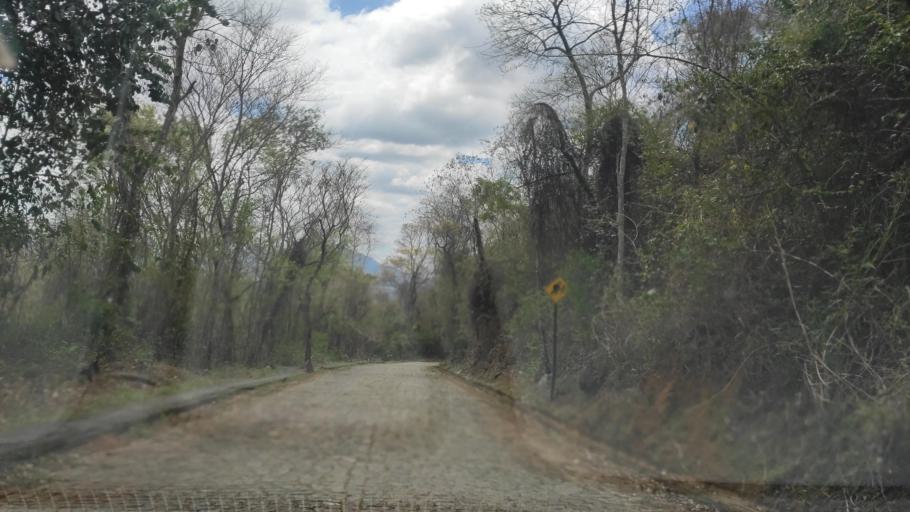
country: BR
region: Espirito Santo
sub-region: Vitoria
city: Vitoria
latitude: -20.2995
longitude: -40.3383
